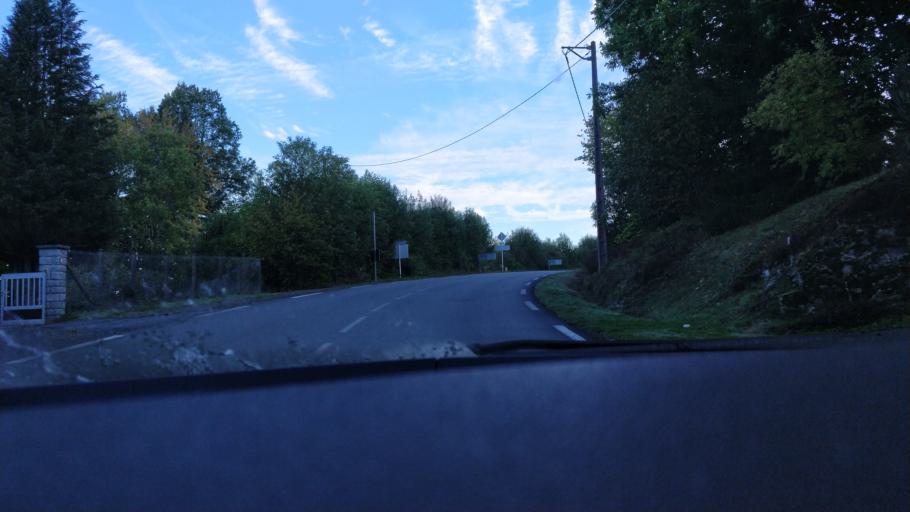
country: FR
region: Limousin
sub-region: Departement de la Haute-Vienne
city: Sauviat-sur-Vige
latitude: 45.9206
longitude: 1.6401
